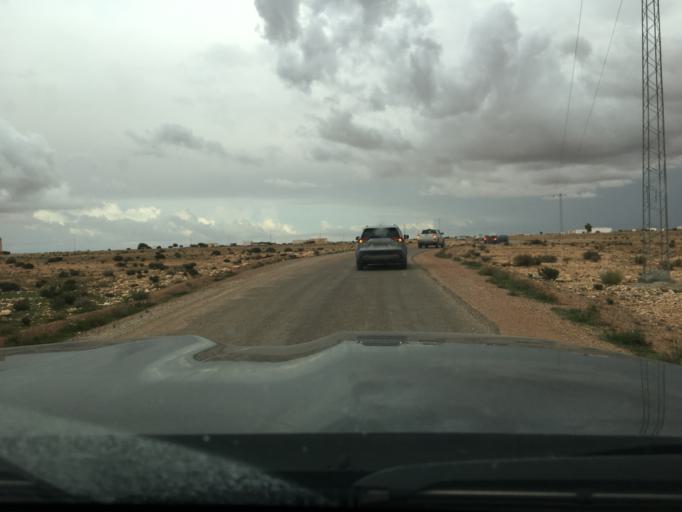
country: TN
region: Madanin
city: Medenine
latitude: 33.2892
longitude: 10.6049
